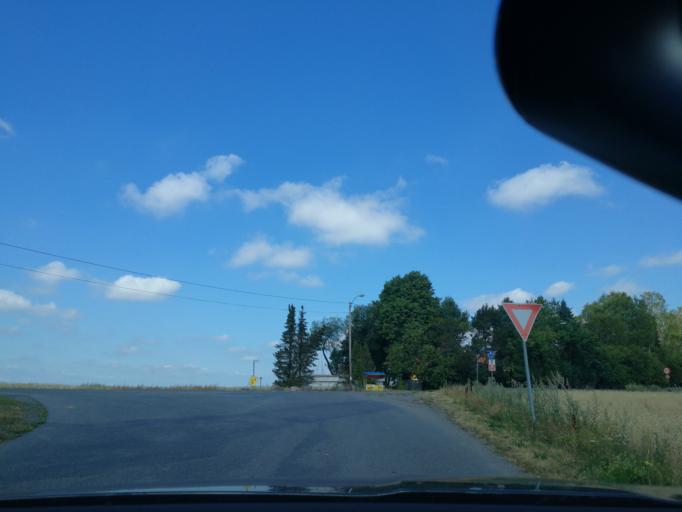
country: NO
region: Vestfold
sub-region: Sandefjord
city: Sandefjord
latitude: 59.1556
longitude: 10.1998
